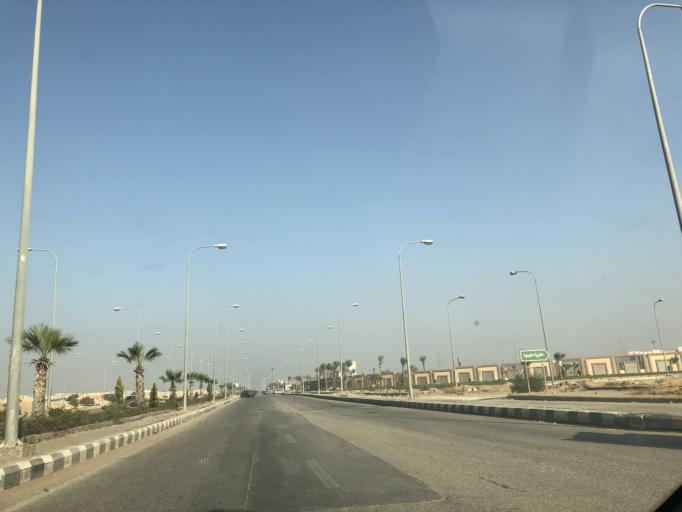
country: EG
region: Al Jizah
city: Madinat Sittah Uktubar
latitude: 29.9435
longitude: 31.0600
